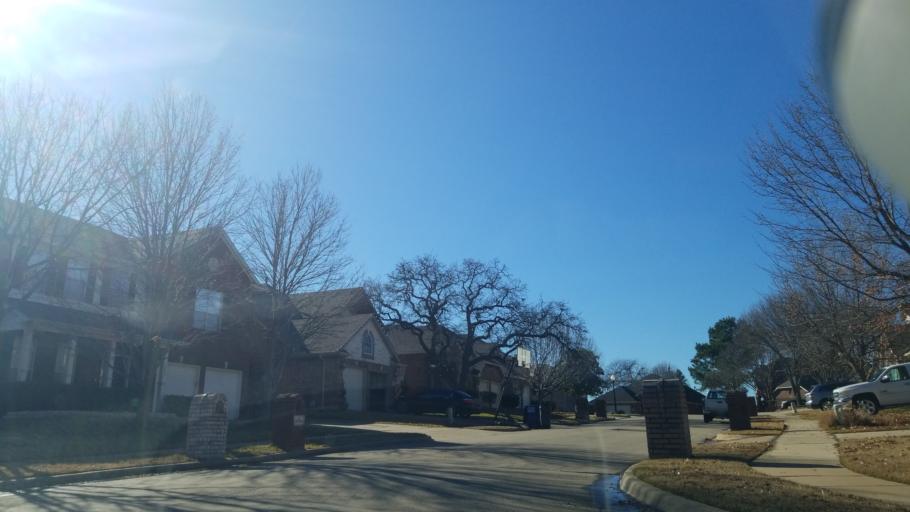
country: US
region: Texas
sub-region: Denton County
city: Corinth
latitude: 33.1509
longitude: -97.0856
